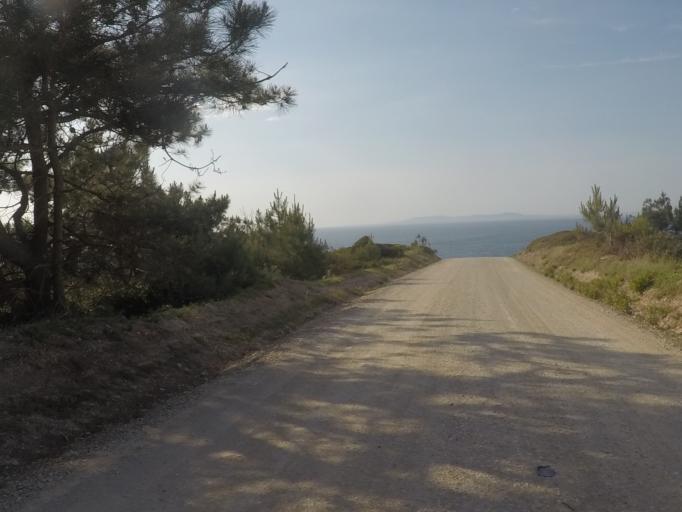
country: PT
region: Setubal
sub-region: Sesimbra
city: Sesimbra
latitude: 38.4483
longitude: -9.1999
